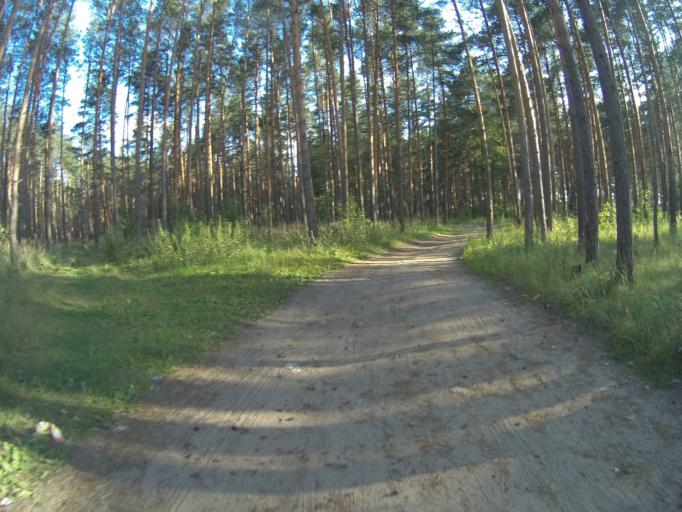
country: RU
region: Vladimir
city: Kommunar
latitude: 56.1200
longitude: 40.4609
